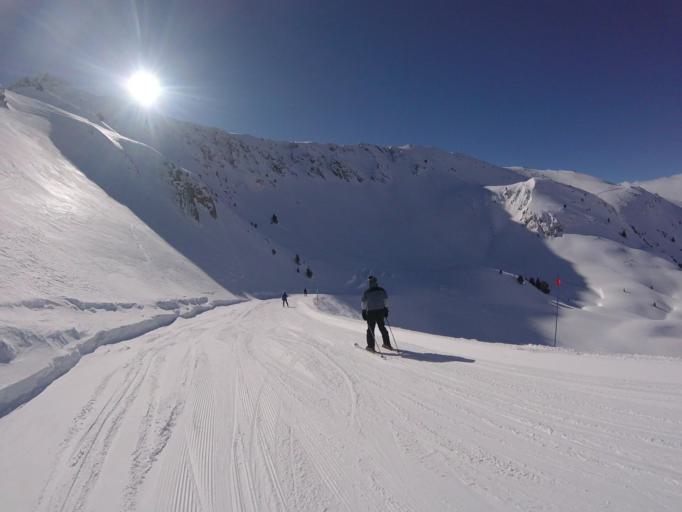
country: ES
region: Catalonia
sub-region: Provincia de Lleida
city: Espot
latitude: 42.7150
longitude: 0.9852
